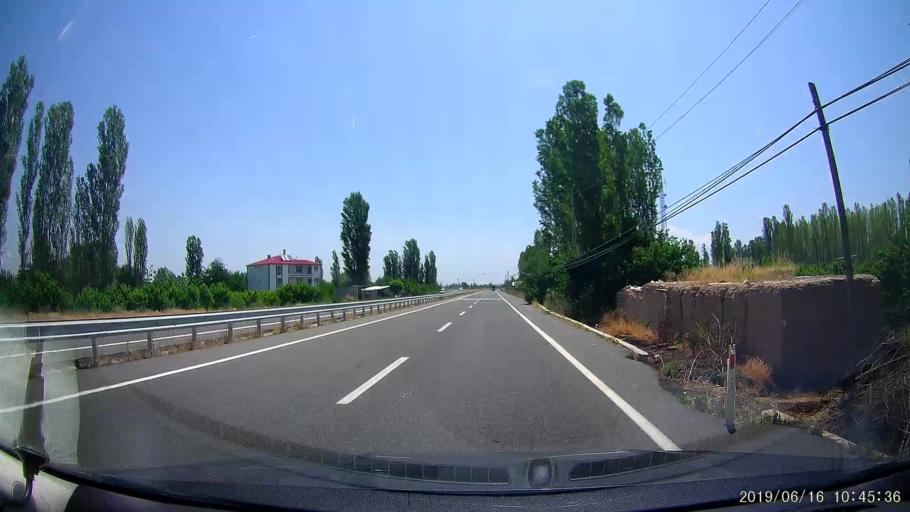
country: AM
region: Armavir
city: Shenavan
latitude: 40.0271
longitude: 43.8711
